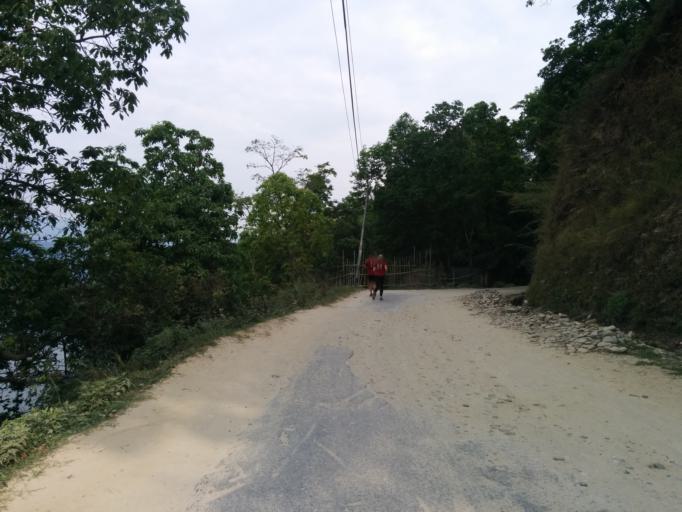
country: NP
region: Western Region
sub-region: Gandaki Zone
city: Pokhara
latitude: 28.2209
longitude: 83.9538
